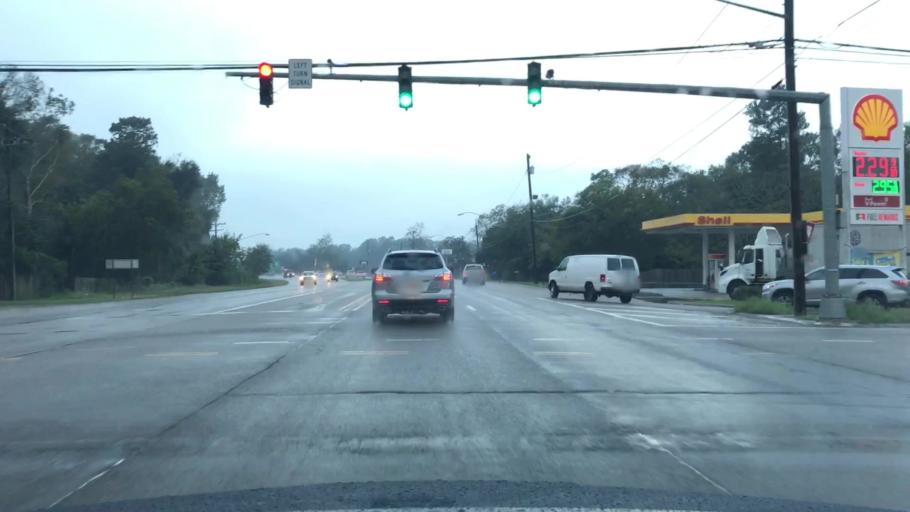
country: US
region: Louisiana
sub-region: Saint Charles Parish
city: Boutte
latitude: 29.9010
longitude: -90.3880
